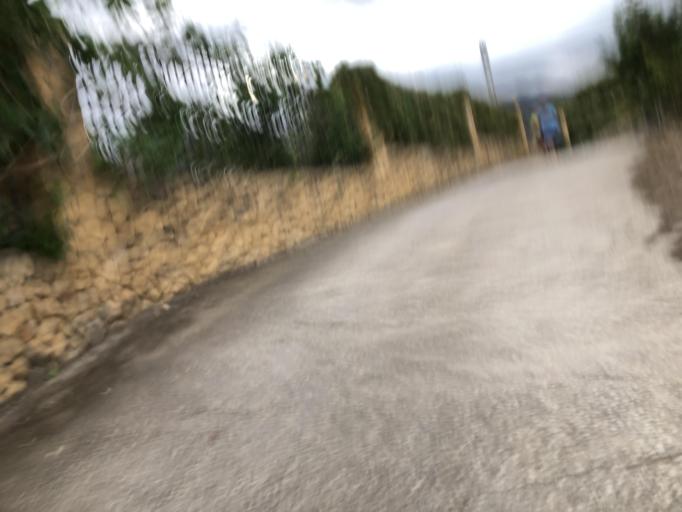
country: ES
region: Valencia
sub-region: Provincia de Alicante
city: Polop
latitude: 38.6352
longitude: -0.1399
